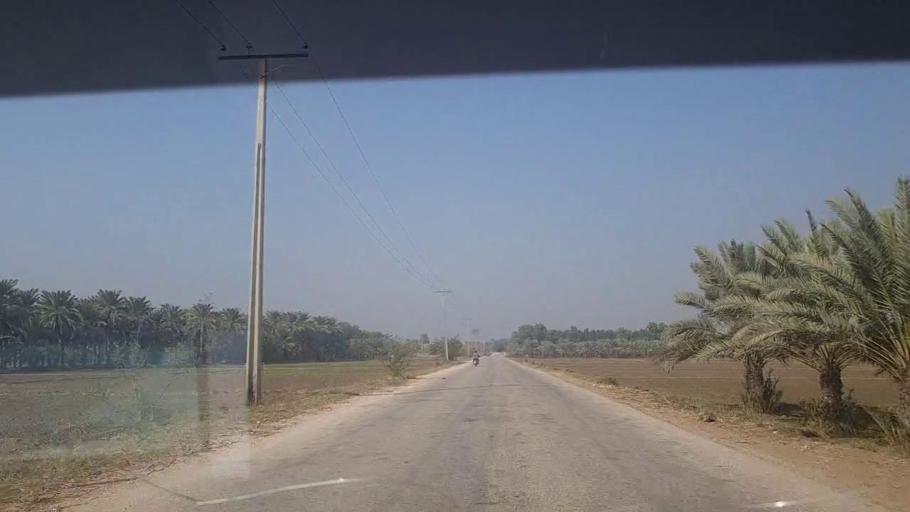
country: PK
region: Sindh
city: Kot Diji
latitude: 27.3677
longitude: 68.7019
